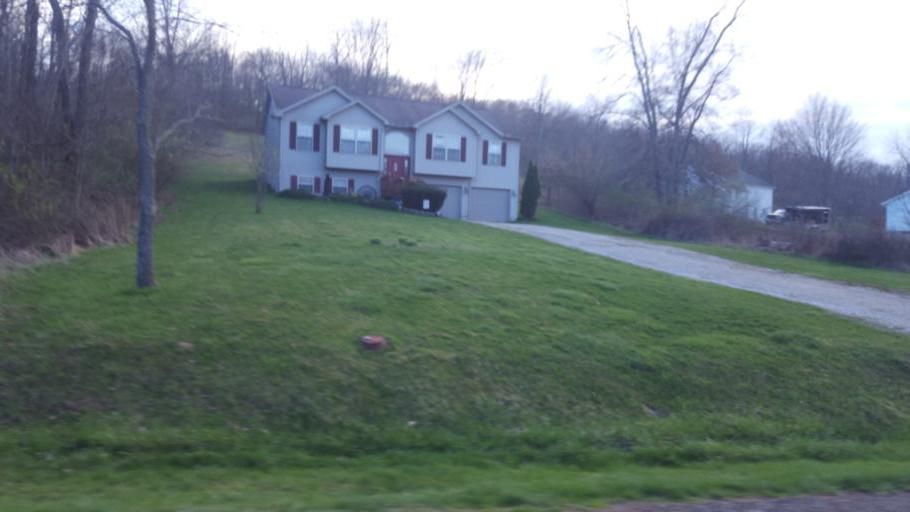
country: US
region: Ohio
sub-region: Knox County
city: Danville
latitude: 40.4570
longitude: -82.3310
